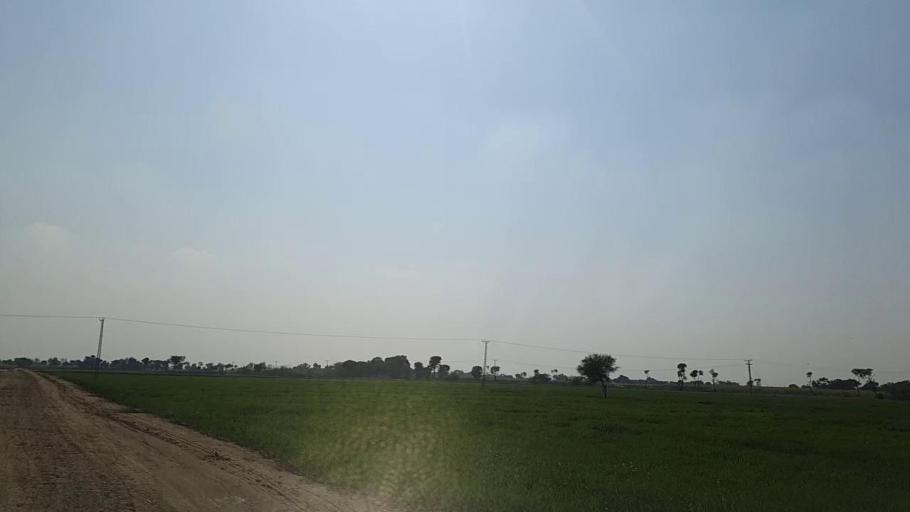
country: PK
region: Sindh
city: Daur
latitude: 26.4440
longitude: 68.2333
